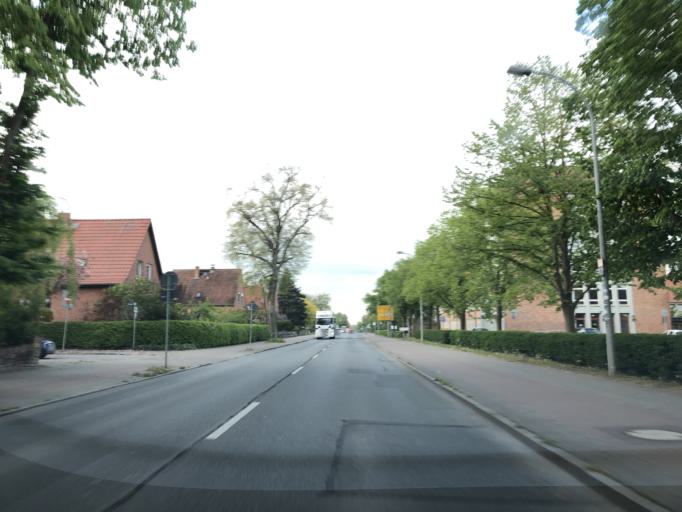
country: DE
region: Mecklenburg-Vorpommern
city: Guestrow
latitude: 53.7834
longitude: 12.1780
